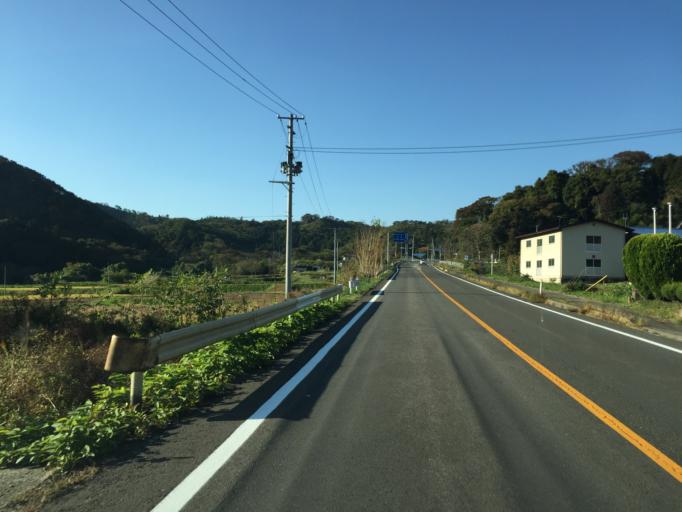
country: JP
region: Fukushima
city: Yanagawamachi-saiwaicho
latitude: 37.9150
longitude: 140.5923
